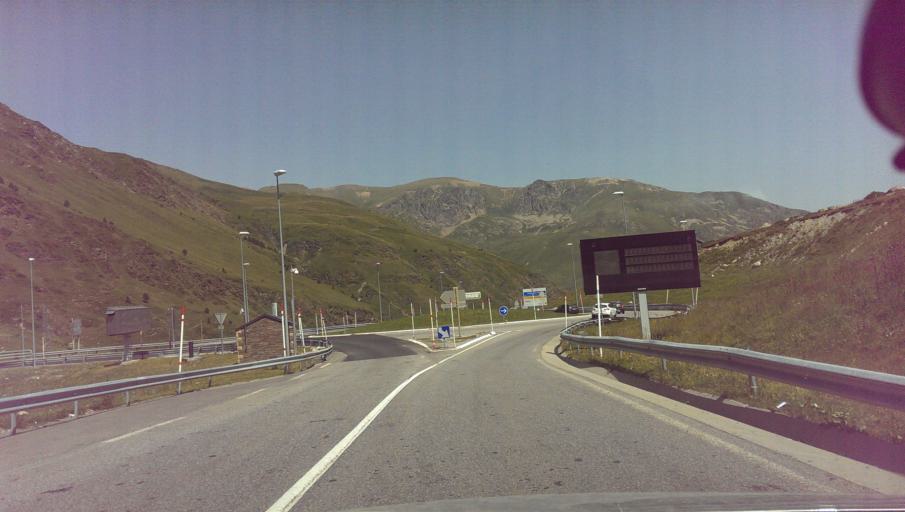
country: AD
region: Encamp
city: Pas de la Casa
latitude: 42.5484
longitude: 1.7378
